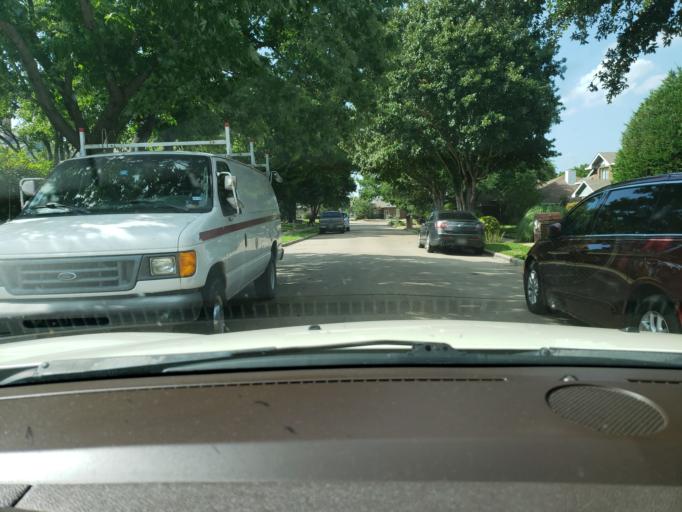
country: US
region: Texas
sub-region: Dallas County
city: Rowlett
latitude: 32.8978
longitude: -96.5743
